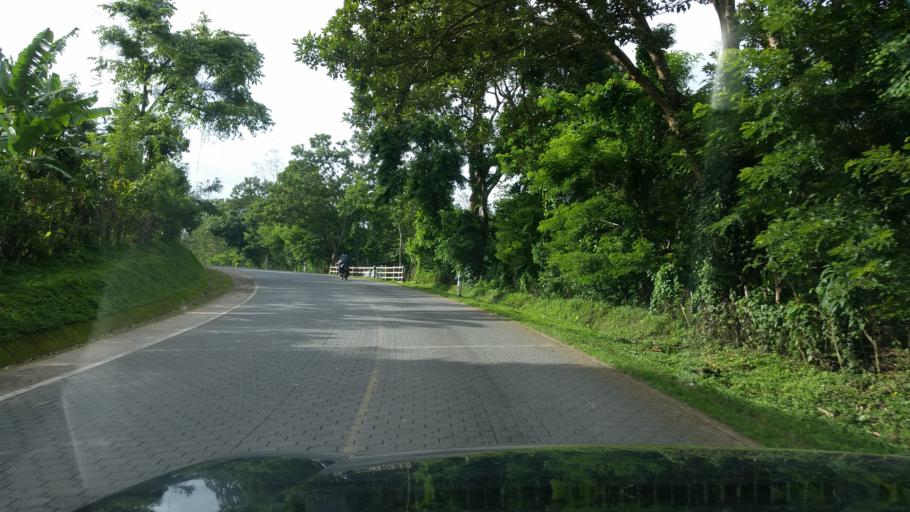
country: NI
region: Matagalpa
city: San Ramon
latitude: 13.1660
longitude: -85.7272
